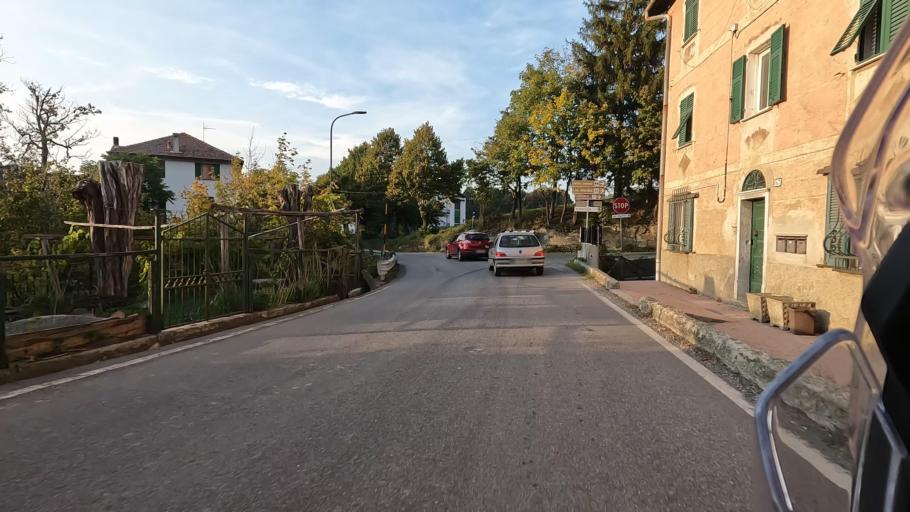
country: IT
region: Liguria
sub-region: Provincia di Savona
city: Sassello
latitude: 44.4754
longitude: 8.4870
